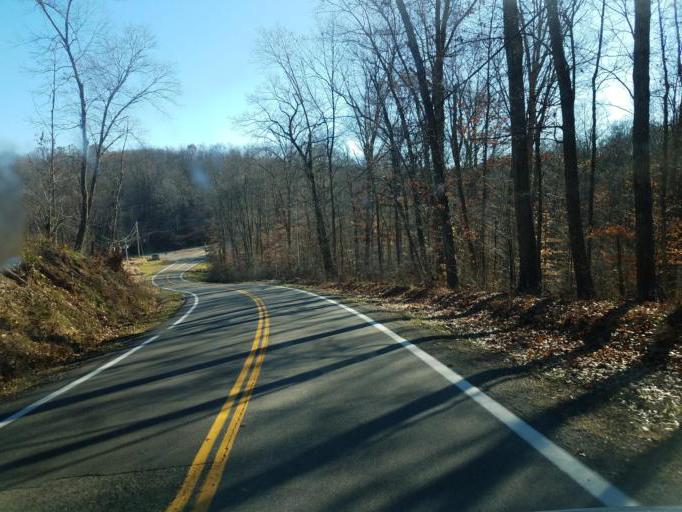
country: US
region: Ohio
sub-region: Muskingum County
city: Frazeysburg
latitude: 40.2628
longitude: -82.0862
